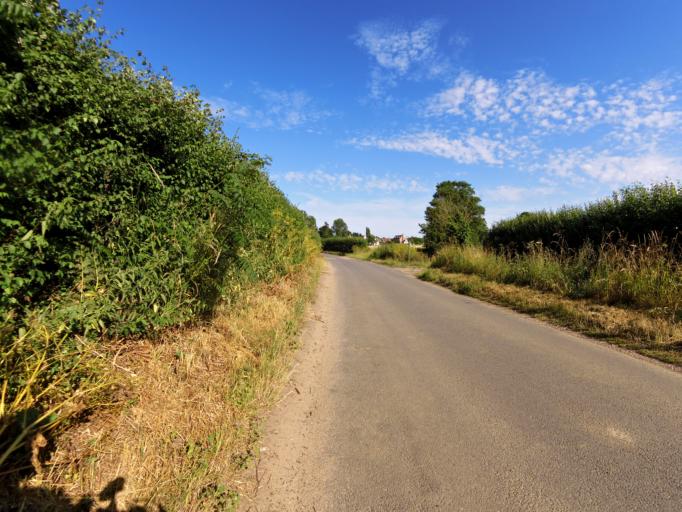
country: GB
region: England
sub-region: Suffolk
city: Leiston
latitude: 52.2693
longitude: 1.5698
